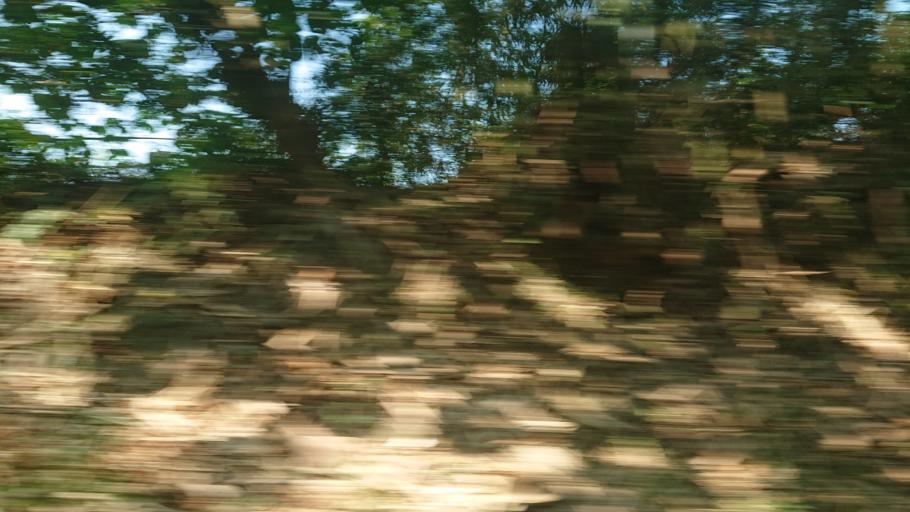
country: TW
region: Taiwan
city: Lugu
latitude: 23.7180
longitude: 120.6695
